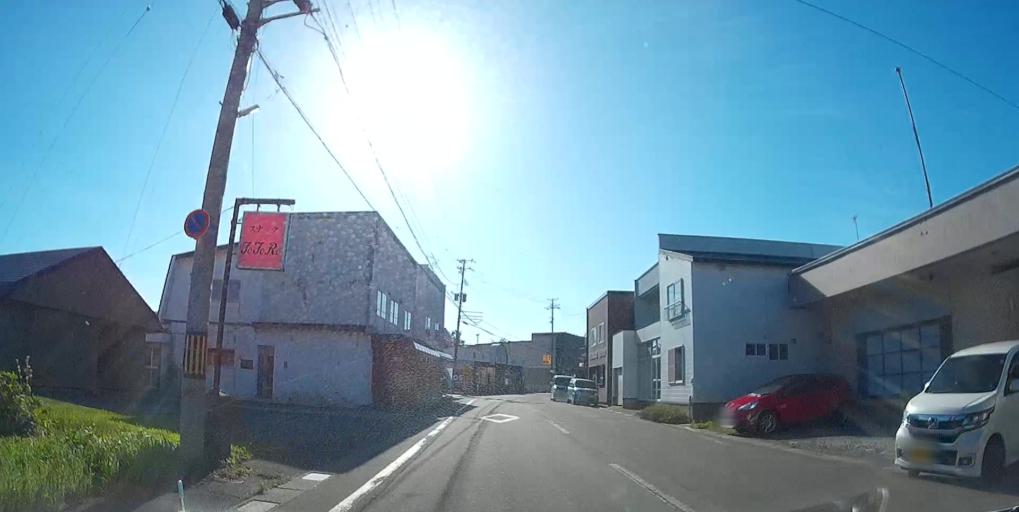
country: JP
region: Hokkaido
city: Kamiiso
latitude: 42.2252
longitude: 139.8221
